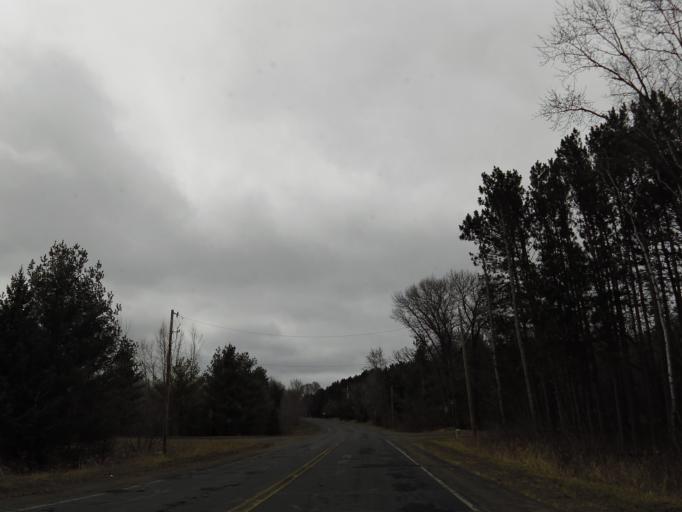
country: US
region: Minnesota
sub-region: Washington County
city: Oak Park Heights
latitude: 45.0160
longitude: -92.8282
